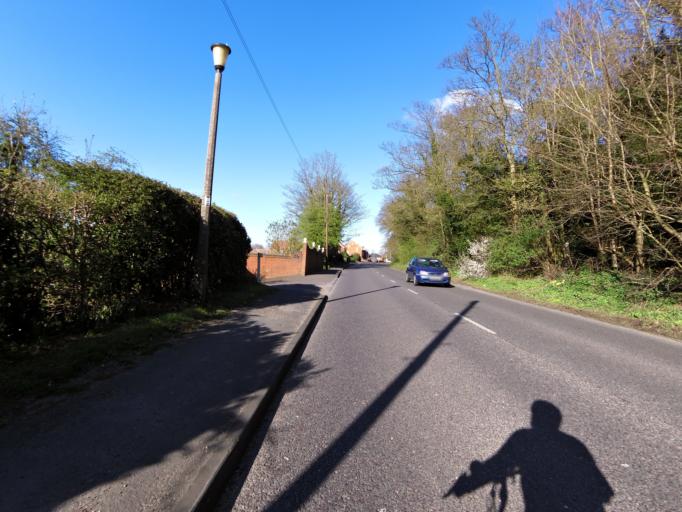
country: GB
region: England
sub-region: Suffolk
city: Bramford
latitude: 52.0553
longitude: 1.1155
